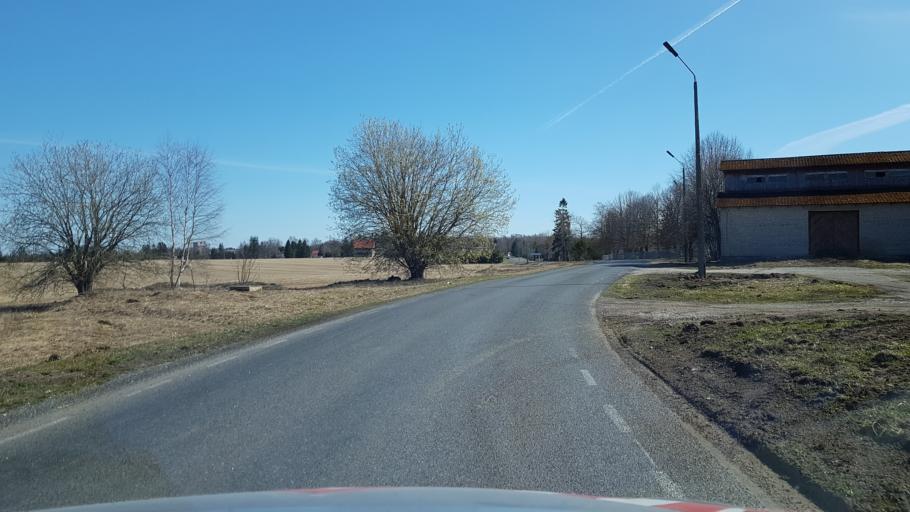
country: EE
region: Laeaene-Virumaa
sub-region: Vinni vald
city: Vinni
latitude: 59.2838
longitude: 26.3993
